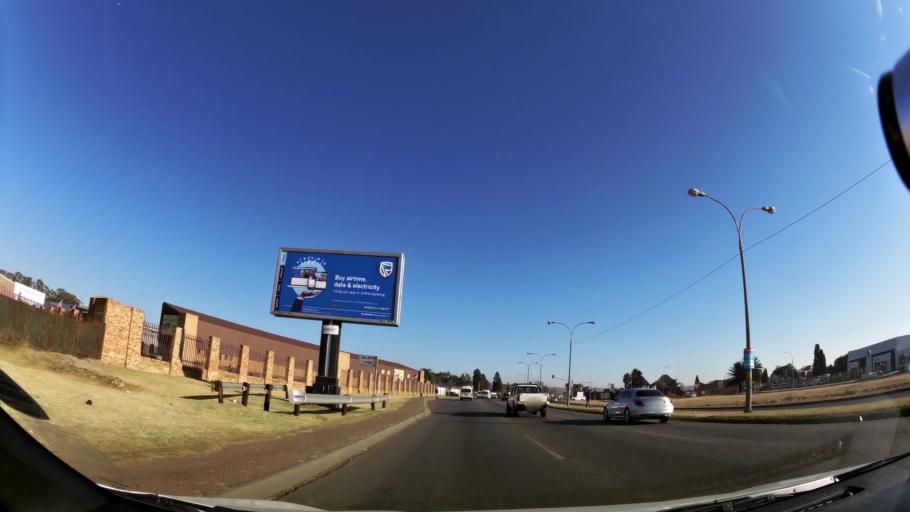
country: ZA
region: Gauteng
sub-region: Ekurhuleni Metropolitan Municipality
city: Germiston
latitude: -26.2872
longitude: 28.1345
